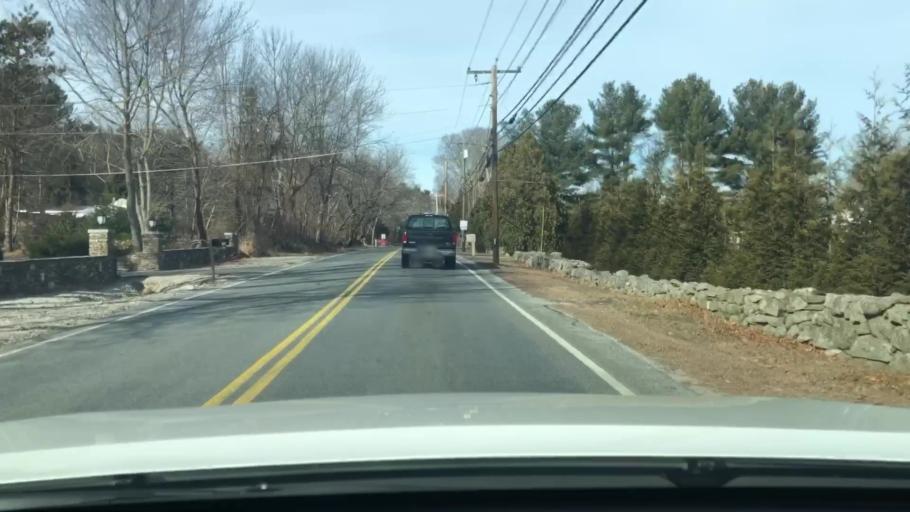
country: US
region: Massachusetts
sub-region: Worcester County
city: Mendon
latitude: 42.0891
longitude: -71.5330
